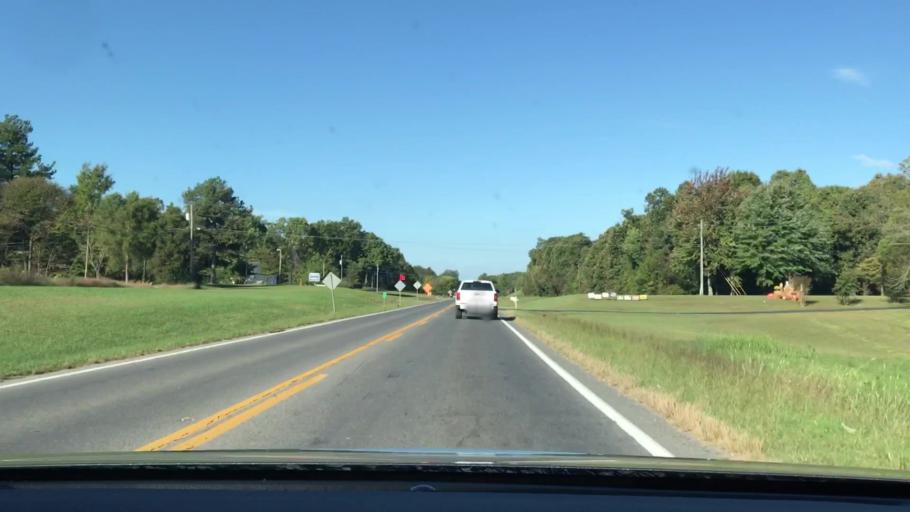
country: US
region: Kentucky
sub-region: Marshall County
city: Calvert City
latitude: 37.0042
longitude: -88.3569
